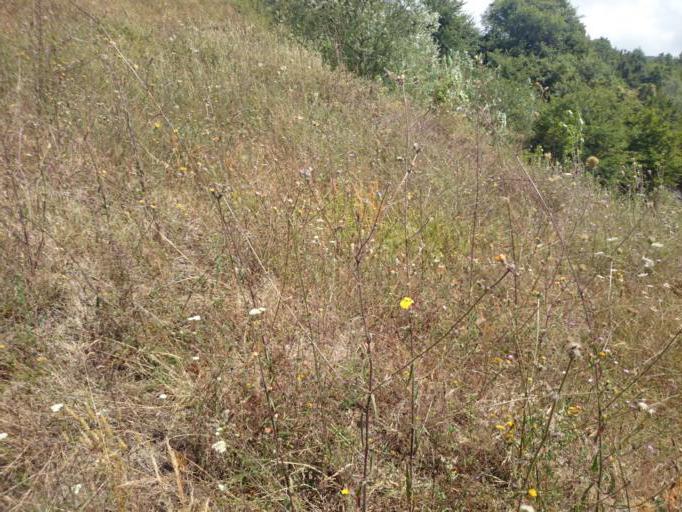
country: AL
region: Elbasan
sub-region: Rrethi i Elbasanit
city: Shushice
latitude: 41.0612
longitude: 20.1473
